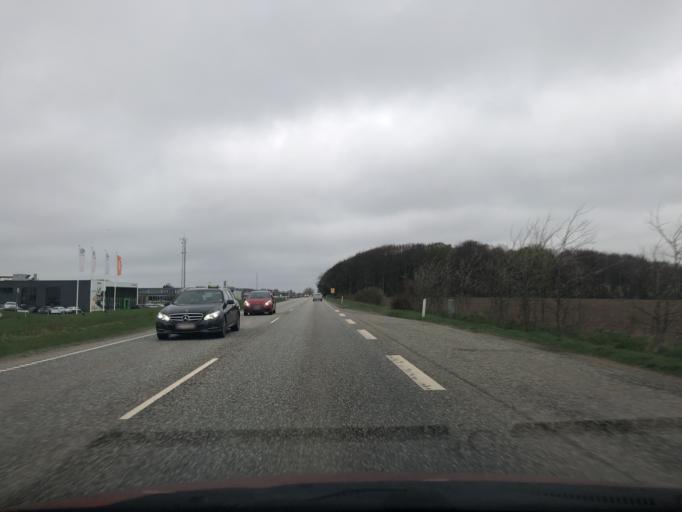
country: DK
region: Central Jutland
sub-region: Holstebro Kommune
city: Holstebro
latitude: 56.3382
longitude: 8.6433
